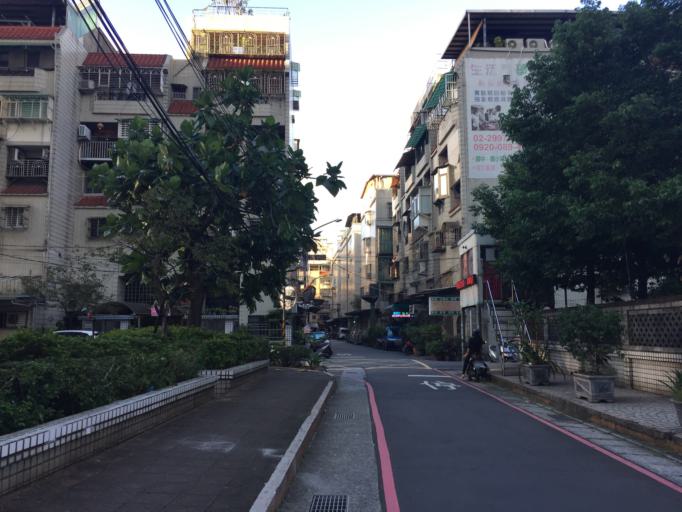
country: TW
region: Taipei
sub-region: Taipei
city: Banqiao
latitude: 25.0496
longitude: 121.4498
